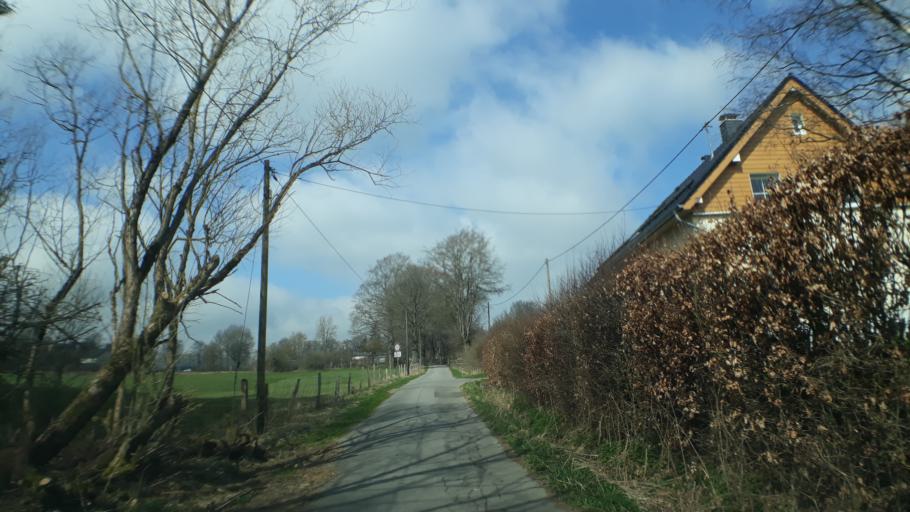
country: DE
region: North Rhine-Westphalia
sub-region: Regierungsbezirk Koln
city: Monschau
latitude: 50.5653
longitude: 6.2583
